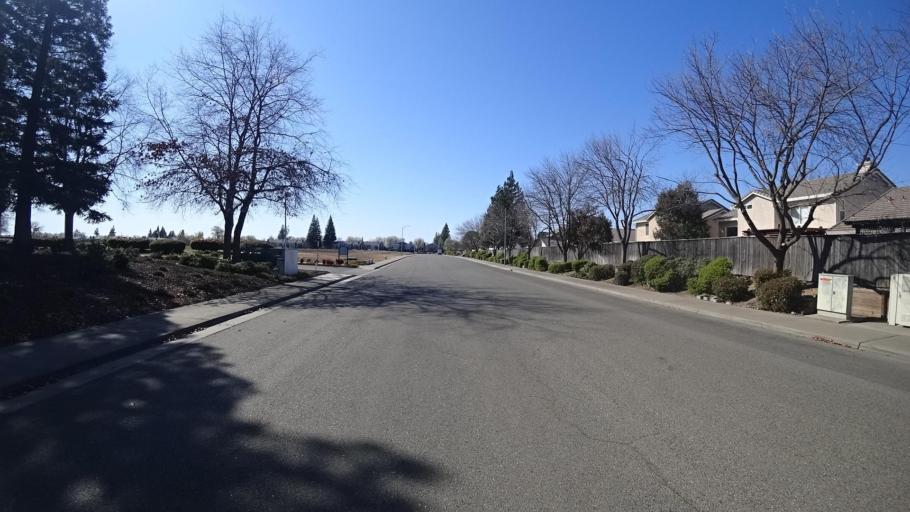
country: US
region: California
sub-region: Sacramento County
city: Rancho Cordova
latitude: 38.5784
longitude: -121.2923
